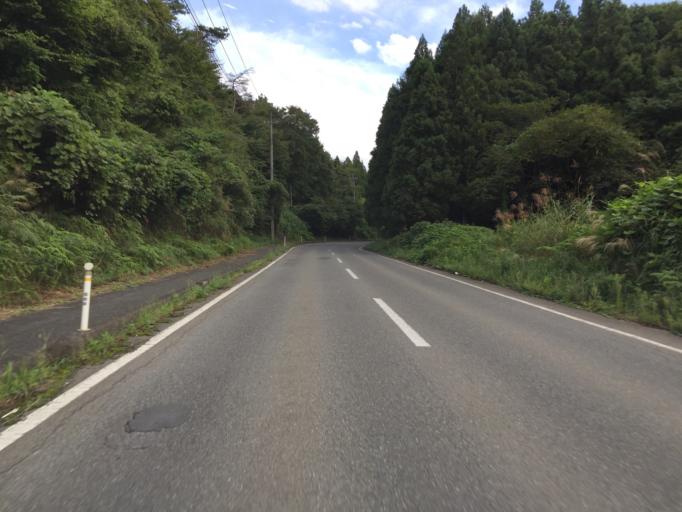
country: JP
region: Fukushima
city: Hobaramachi
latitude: 37.7915
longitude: 140.5418
